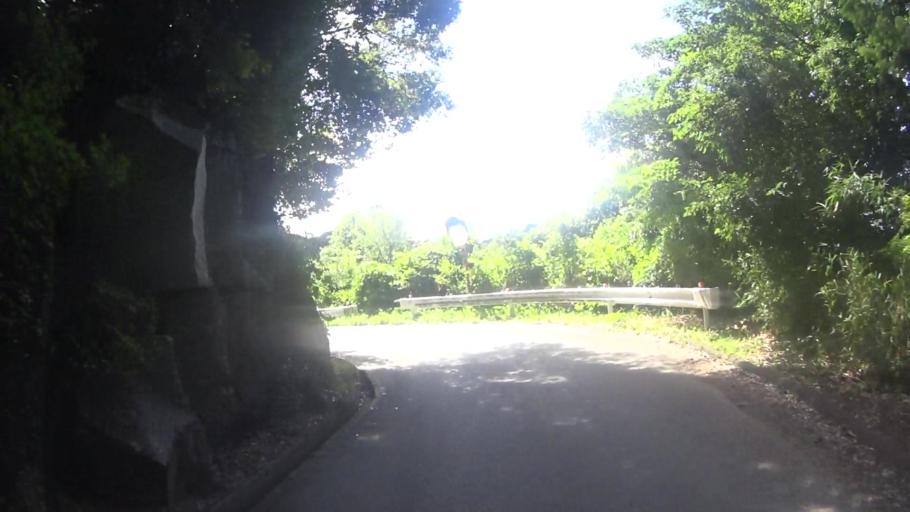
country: JP
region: Nara
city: Nara-shi
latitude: 34.7443
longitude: 135.9467
